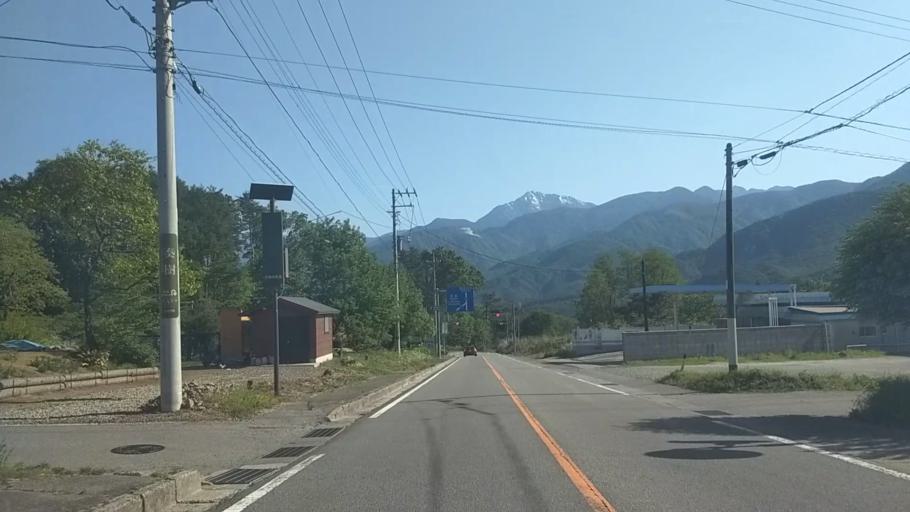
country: JP
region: Nagano
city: Chino
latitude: 35.8621
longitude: 138.2978
